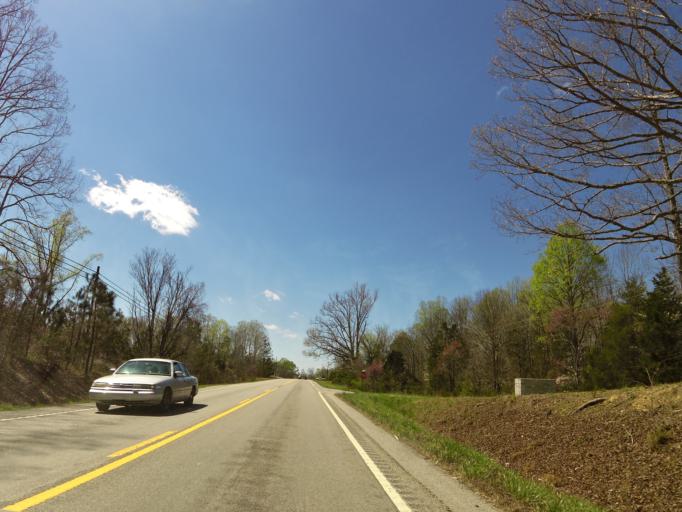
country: US
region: Tennessee
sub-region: DeKalb County
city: Smithville
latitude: 35.9768
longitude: -85.6936
